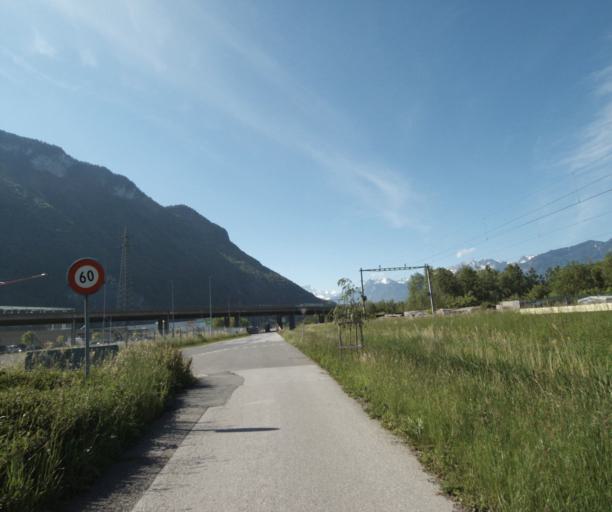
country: CH
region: Vaud
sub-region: Aigle District
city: Villeneuve
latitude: 46.3880
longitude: 6.9285
